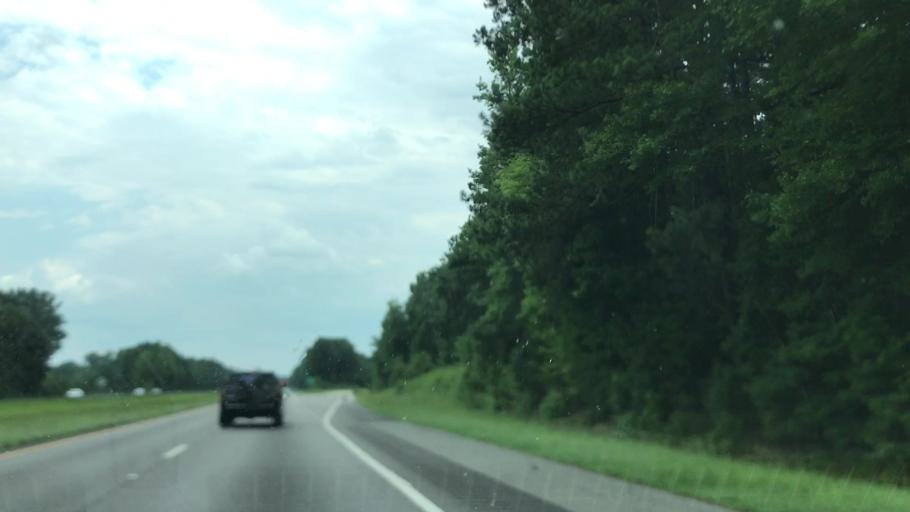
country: US
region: South Carolina
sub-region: Richland County
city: Blythewood
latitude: 34.2896
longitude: -80.9973
